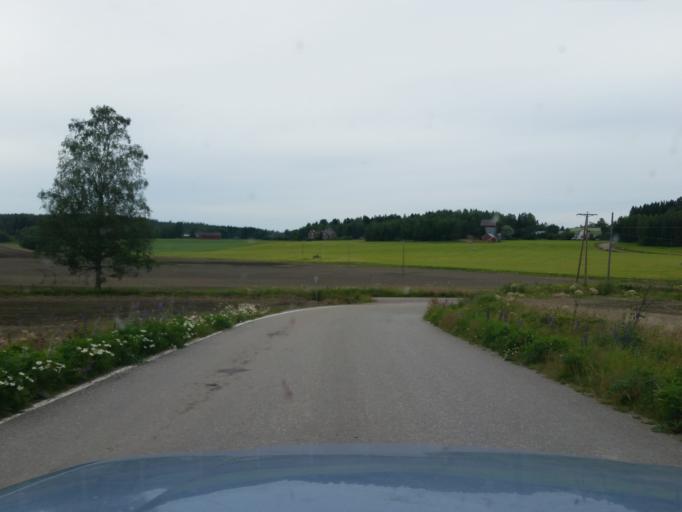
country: FI
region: Uusimaa
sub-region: Helsinki
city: Sammatti
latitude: 60.4739
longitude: 23.8223
